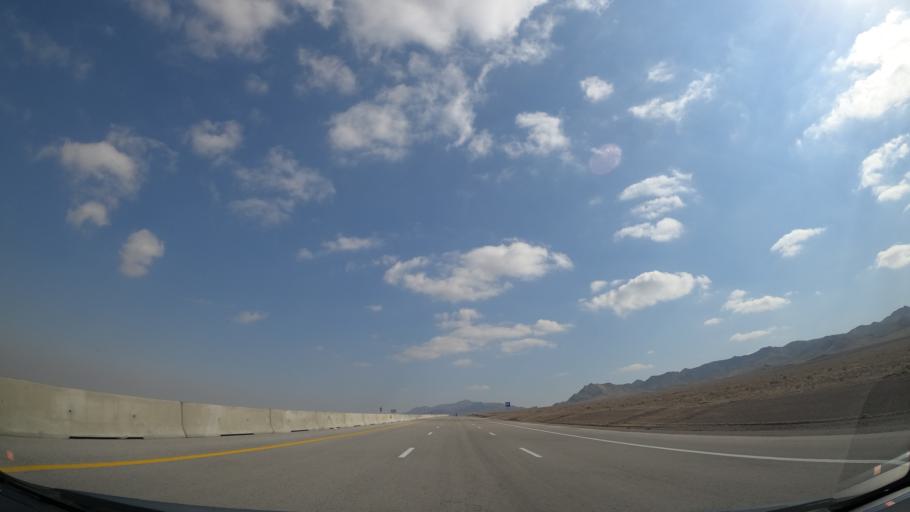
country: IR
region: Alborz
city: Eshtehard
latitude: 35.7124
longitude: 50.5906
